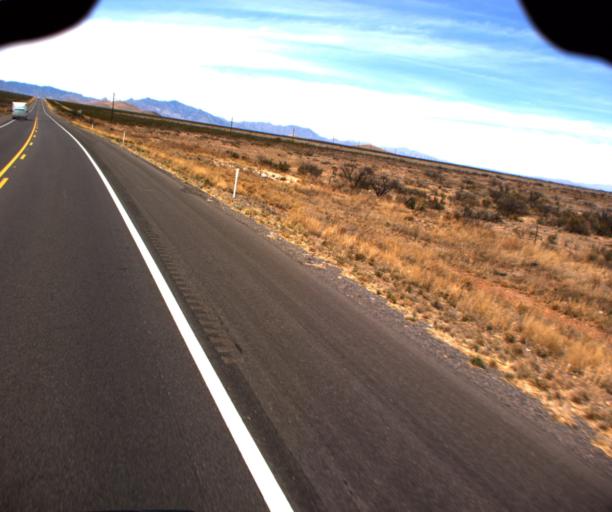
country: US
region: Arizona
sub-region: Cochise County
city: Willcox
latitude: 31.9055
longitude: -109.7217
